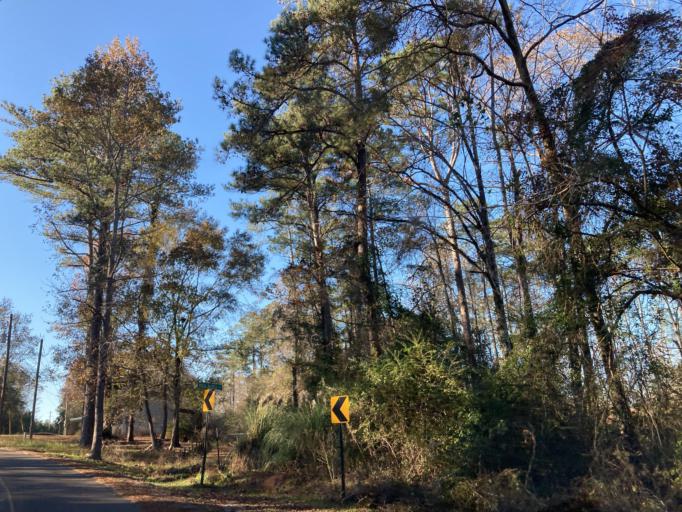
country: US
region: Mississippi
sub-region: Lamar County
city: Sumrall
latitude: 31.4012
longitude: -89.5801
